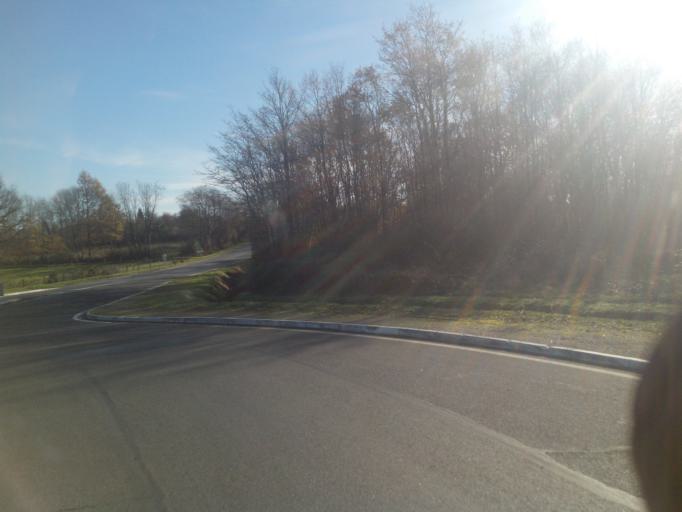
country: FR
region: Limousin
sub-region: Departement de la Haute-Vienne
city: Bussiere-Poitevine
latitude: 46.2698
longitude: 0.8635
